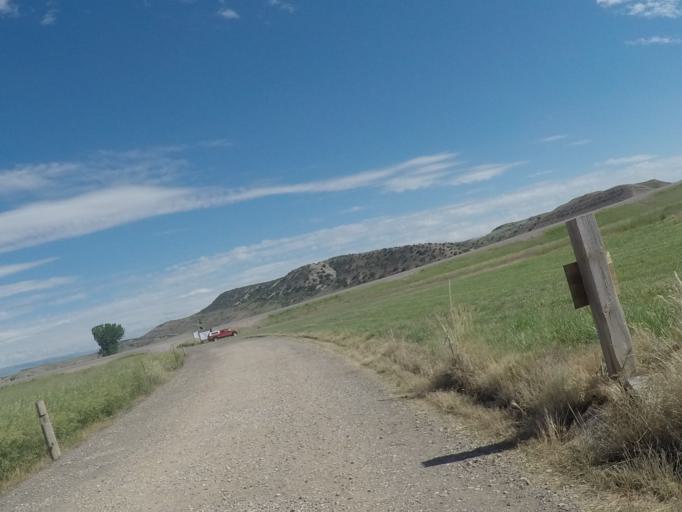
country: US
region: Wyoming
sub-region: Washakie County
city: Worland
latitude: 44.0288
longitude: -107.4682
